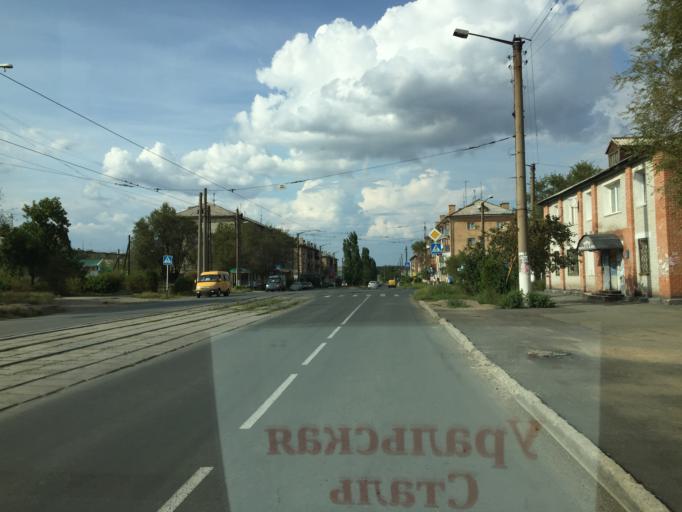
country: RU
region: Orenburg
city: Novotroitsk
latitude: 51.2084
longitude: 58.2995
